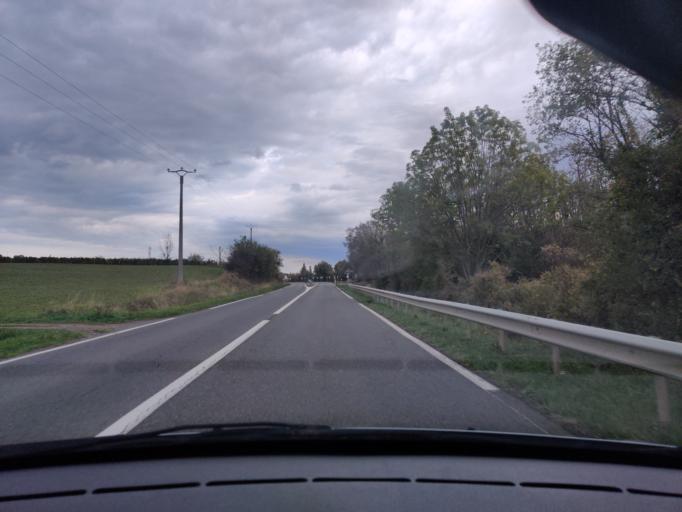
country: FR
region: Auvergne
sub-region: Departement du Puy-de-Dome
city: Combronde
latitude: 45.9637
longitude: 3.1051
